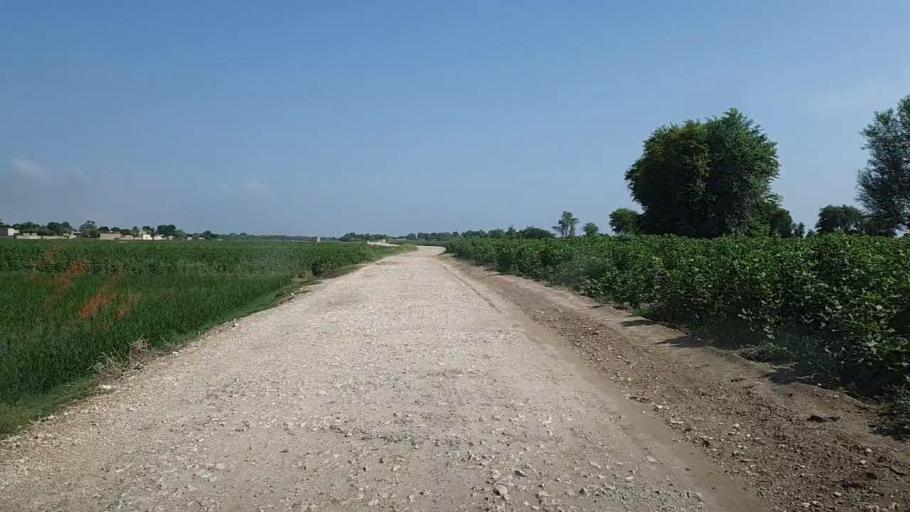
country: PK
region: Sindh
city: Bhiria
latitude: 26.8758
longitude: 68.2310
